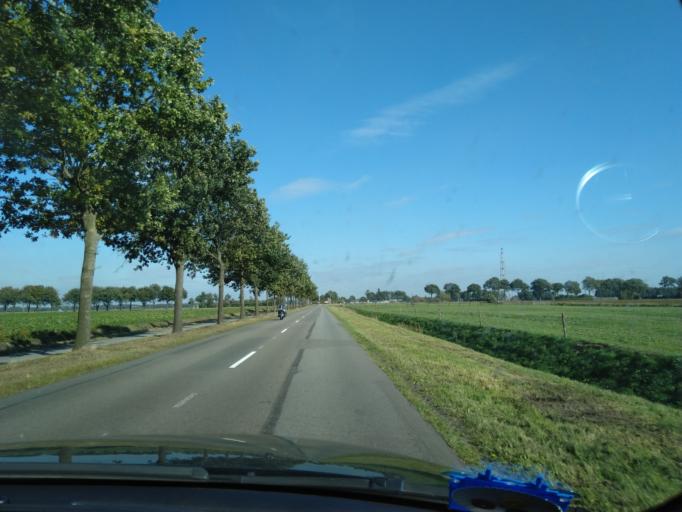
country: NL
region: Groningen
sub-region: Gemeente Hoogezand-Sappemeer
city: Sappemeer
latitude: 53.0900
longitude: 6.8009
